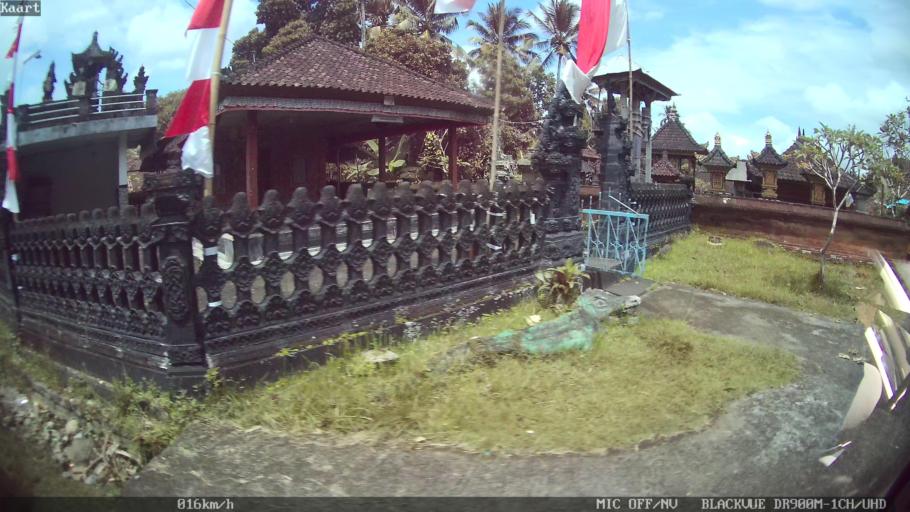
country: ID
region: Bali
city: Banjar Kelodan
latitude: -8.4825
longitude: 115.3683
